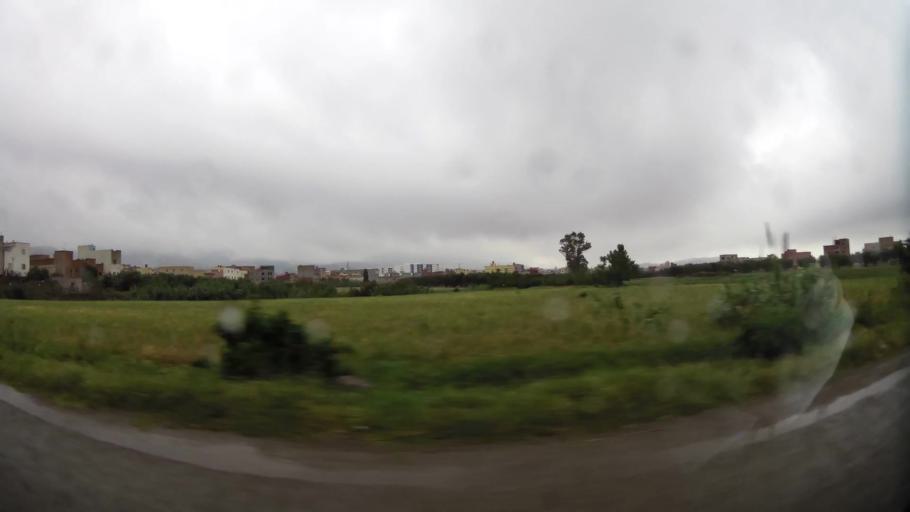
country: MA
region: Oriental
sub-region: Nador
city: Nador
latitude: 35.1532
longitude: -2.9718
